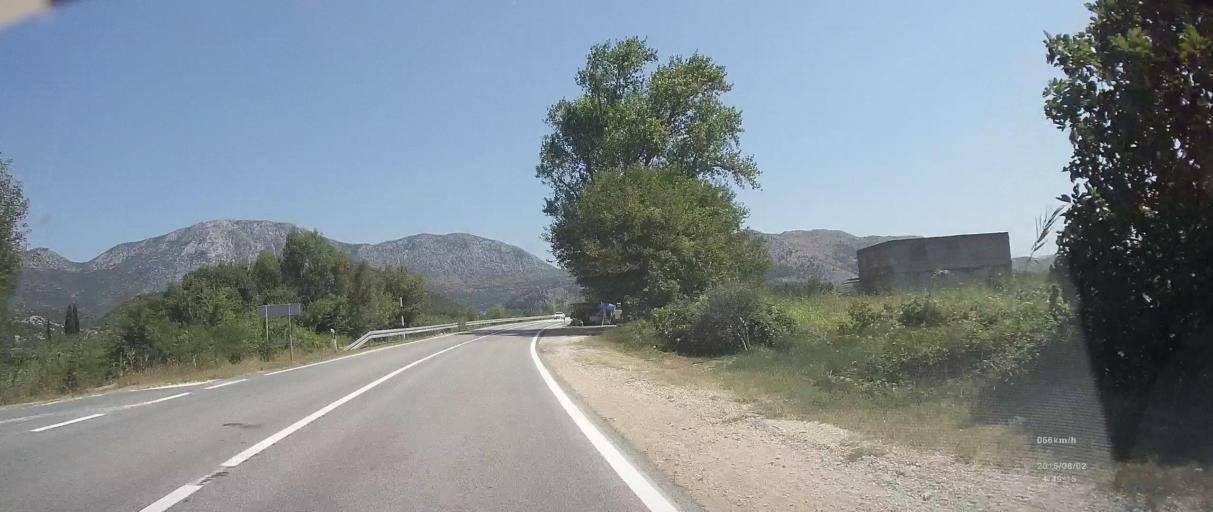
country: HR
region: Dubrovacko-Neretvanska
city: Komin
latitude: 43.0408
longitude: 17.4966
